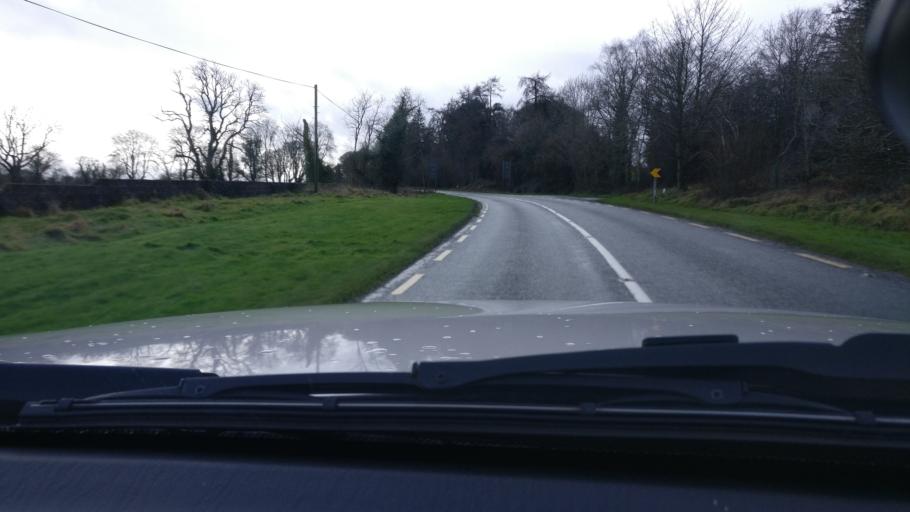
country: IE
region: Leinster
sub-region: An Iarmhi
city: Moate
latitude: 53.6303
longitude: -7.6918
